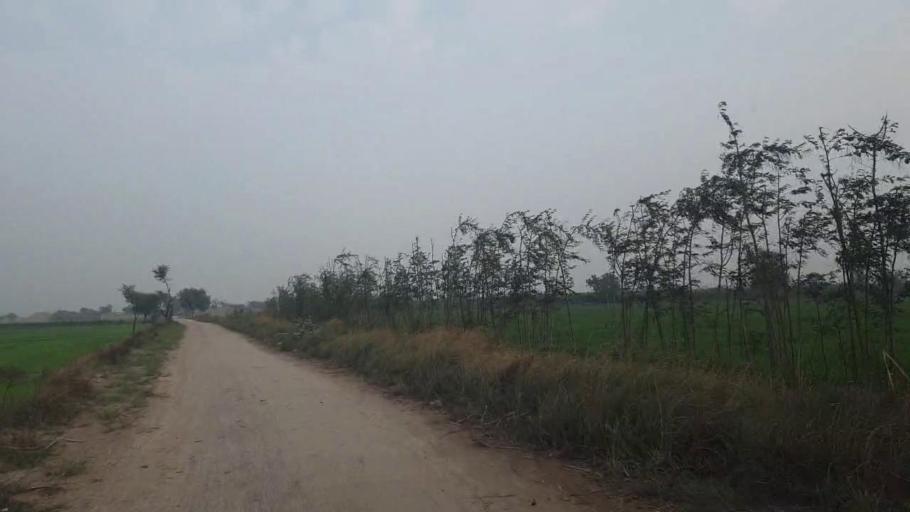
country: PK
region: Sindh
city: Berani
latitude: 25.7970
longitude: 68.7468
